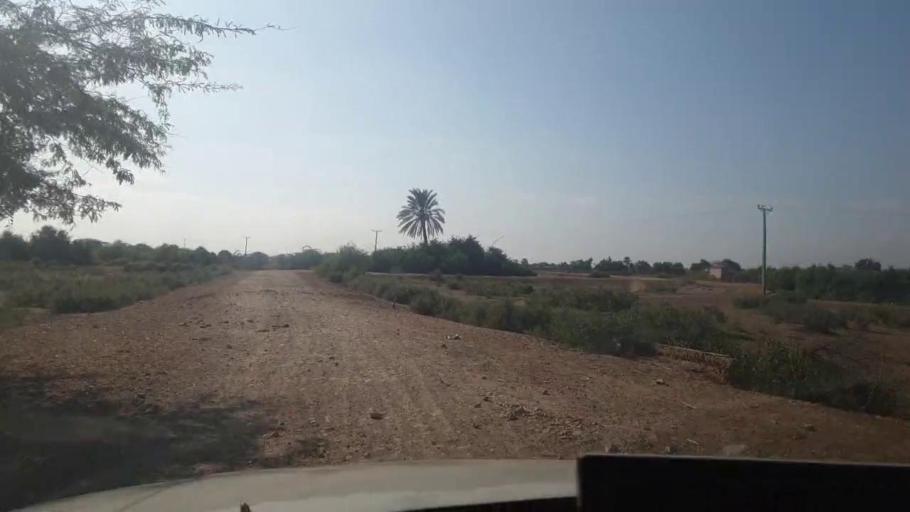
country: PK
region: Sindh
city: Mirpur Sakro
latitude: 24.4709
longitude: 67.5958
